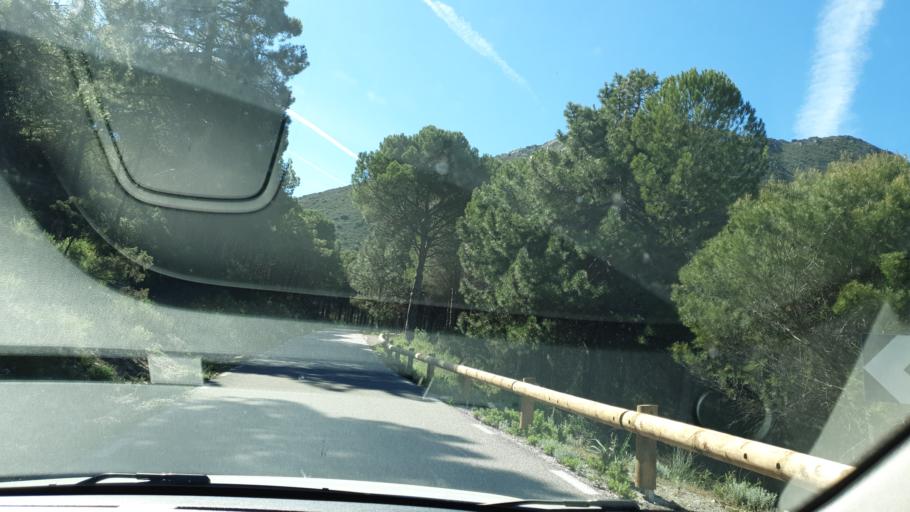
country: ES
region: Andalusia
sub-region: Provincia de Malaga
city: Ojen
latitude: 36.5902
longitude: -4.8580
